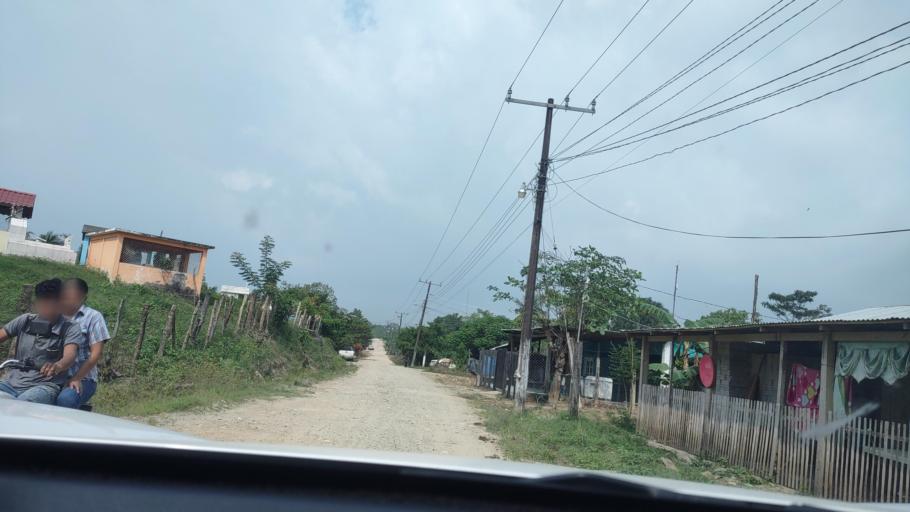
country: MX
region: Veracruz
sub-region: Uxpanapa
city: Poblado 10
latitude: 17.5454
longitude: -94.2880
